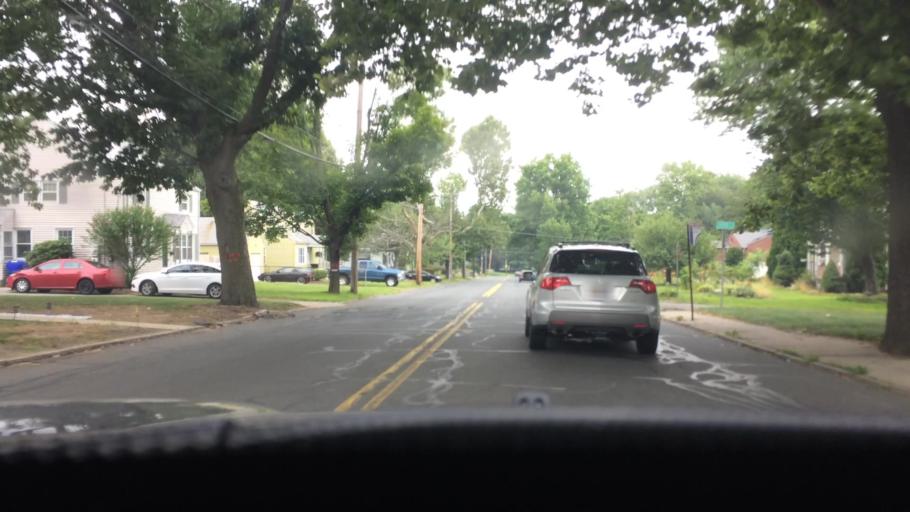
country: US
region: Massachusetts
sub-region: Hampden County
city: Chicopee
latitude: 42.1320
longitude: -72.5847
